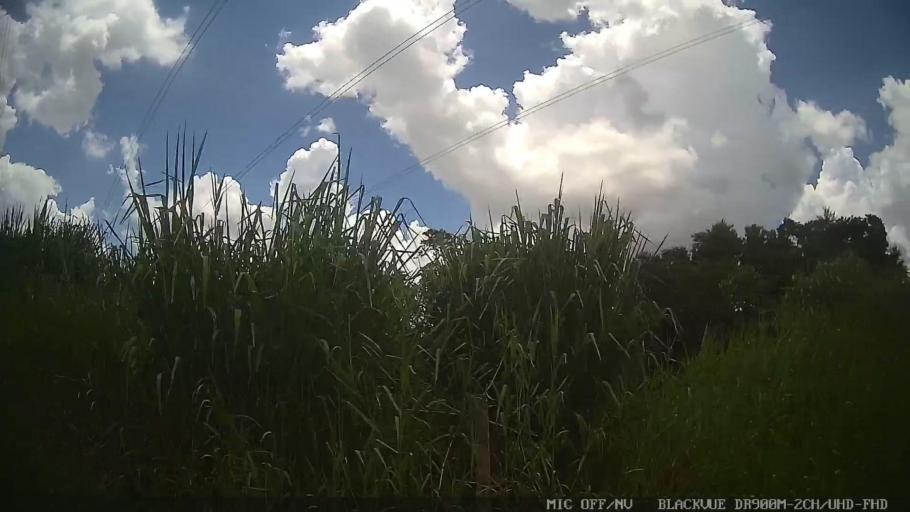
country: BR
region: Sao Paulo
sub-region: Atibaia
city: Atibaia
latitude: -23.1408
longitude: -46.6227
